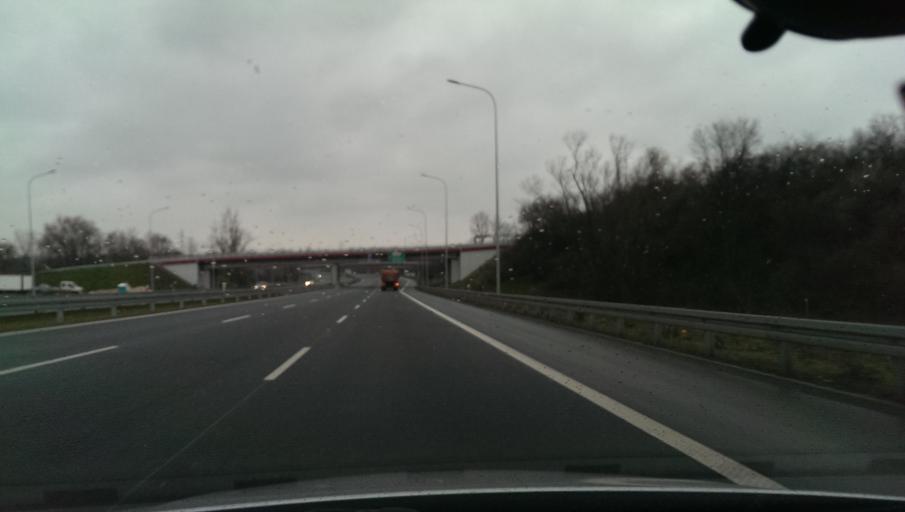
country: PL
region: Lesser Poland Voivodeship
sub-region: Powiat wielicki
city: Kokotow
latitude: 50.0553
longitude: 20.0746
